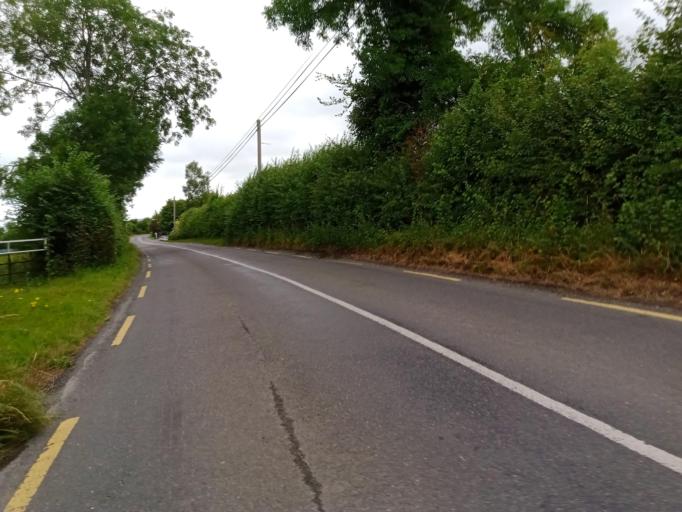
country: IE
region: Leinster
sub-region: Kilkenny
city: Callan
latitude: 52.5667
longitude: -7.4139
